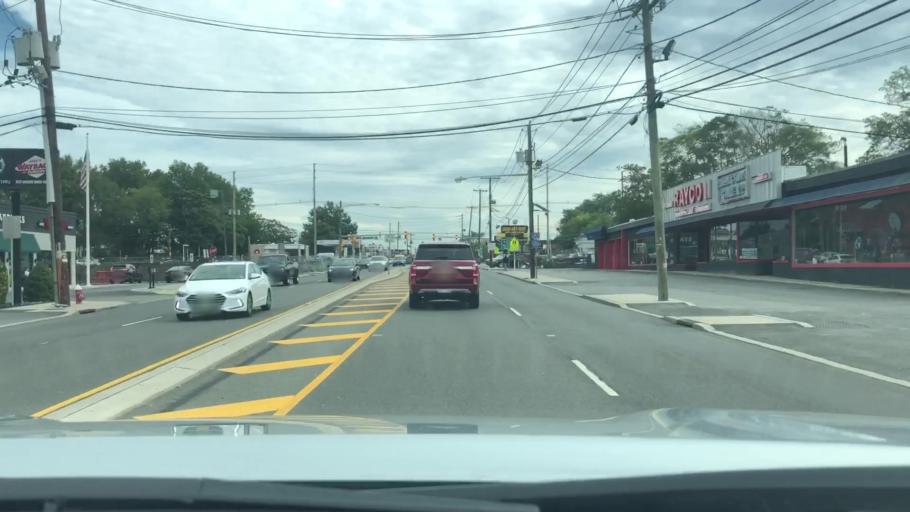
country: US
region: New Jersey
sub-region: Bergen County
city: Little Ferry
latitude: 40.8551
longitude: -74.0441
